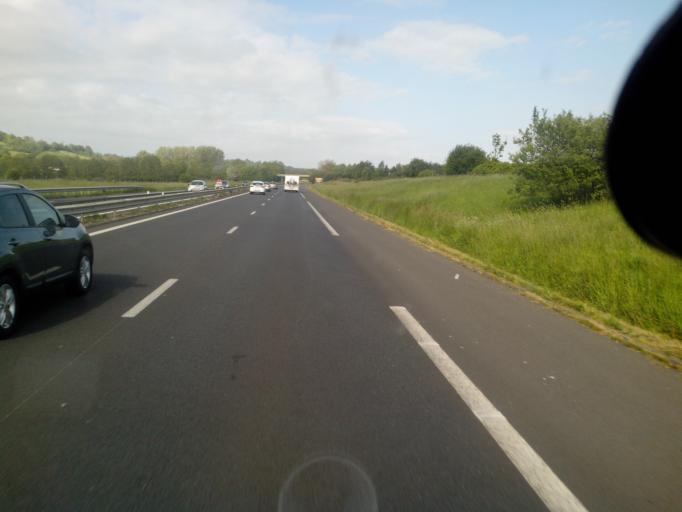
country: FR
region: Lower Normandy
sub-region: Departement du Calvados
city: Dozule
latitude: 49.2437
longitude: -0.0197
